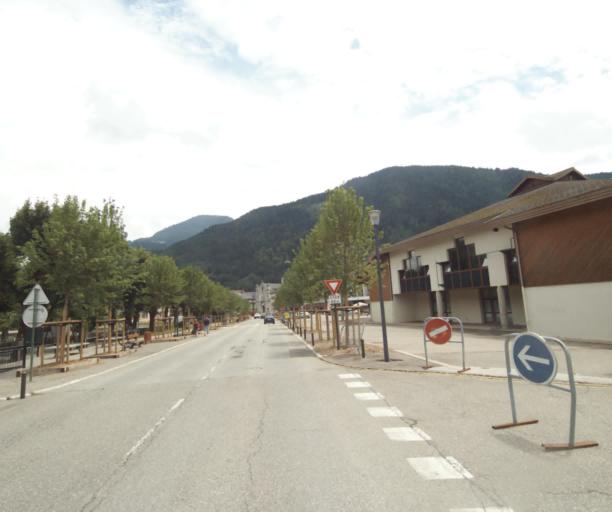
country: FR
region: Rhone-Alpes
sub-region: Departement de la Haute-Savoie
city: Thones
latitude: 45.8820
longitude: 6.3215
